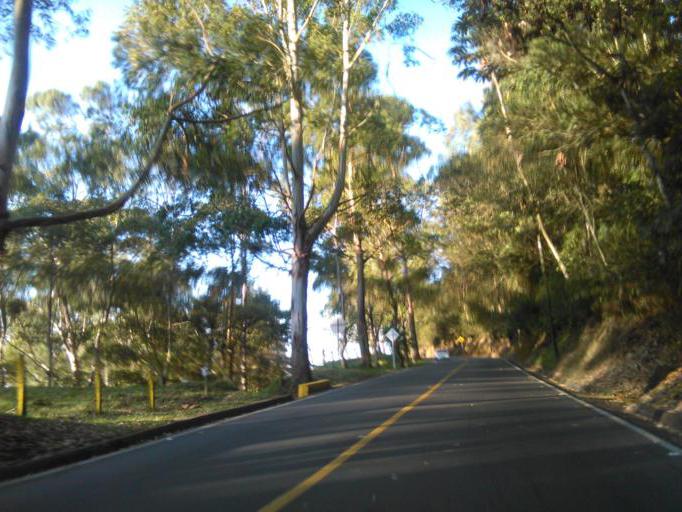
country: CO
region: Antioquia
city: La Ceja
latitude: 6.0048
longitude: -75.4092
